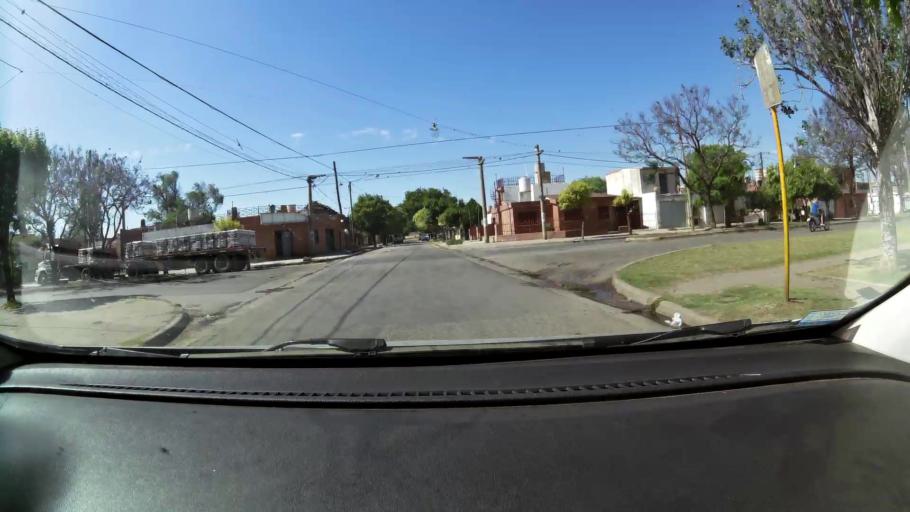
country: AR
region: Cordoba
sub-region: Departamento de Capital
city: Cordoba
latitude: -31.3649
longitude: -64.1494
